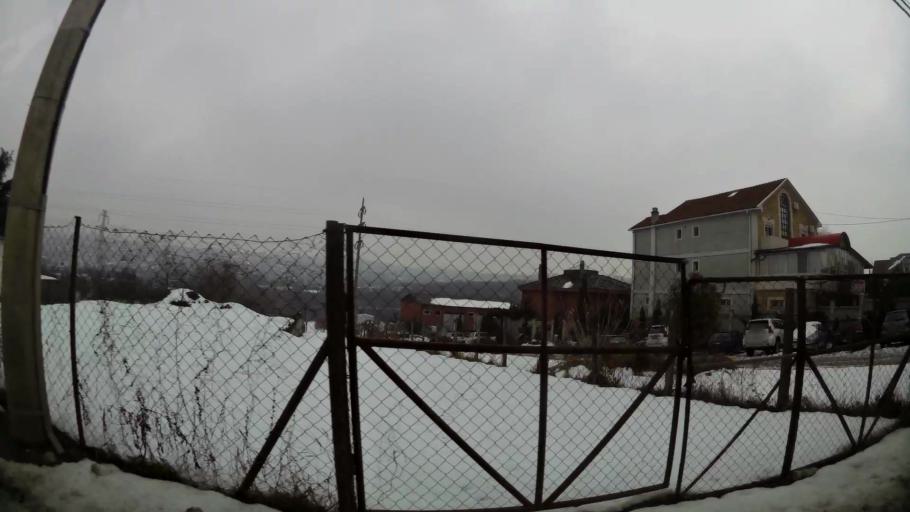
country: RS
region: Central Serbia
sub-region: Belgrade
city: Zvezdara
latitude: 44.7669
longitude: 20.5185
